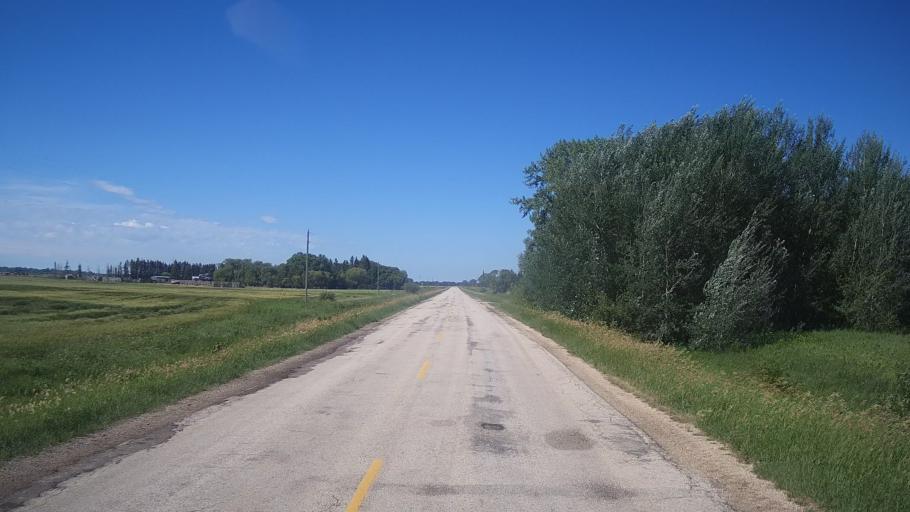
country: CA
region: Manitoba
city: Portage la Prairie
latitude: 50.0397
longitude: -98.0713
